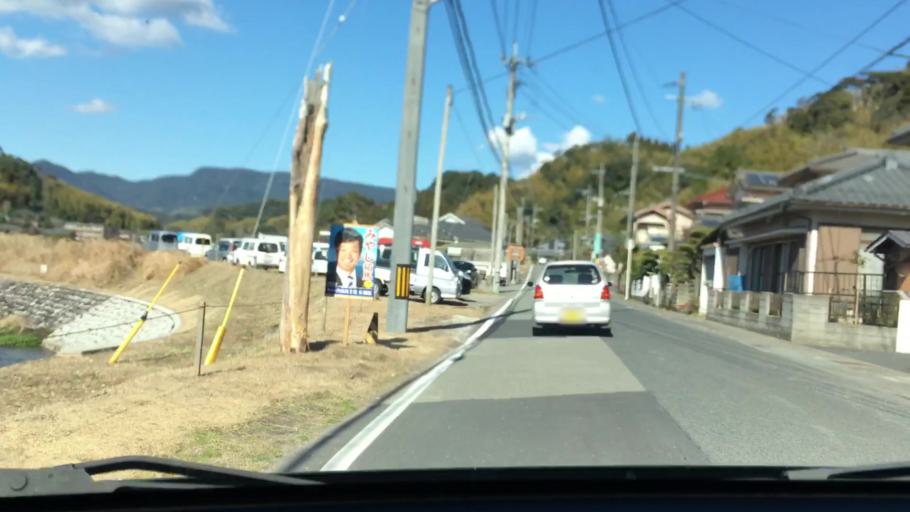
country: JP
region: Kagoshima
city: Ijuin
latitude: 31.6817
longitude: 130.4698
